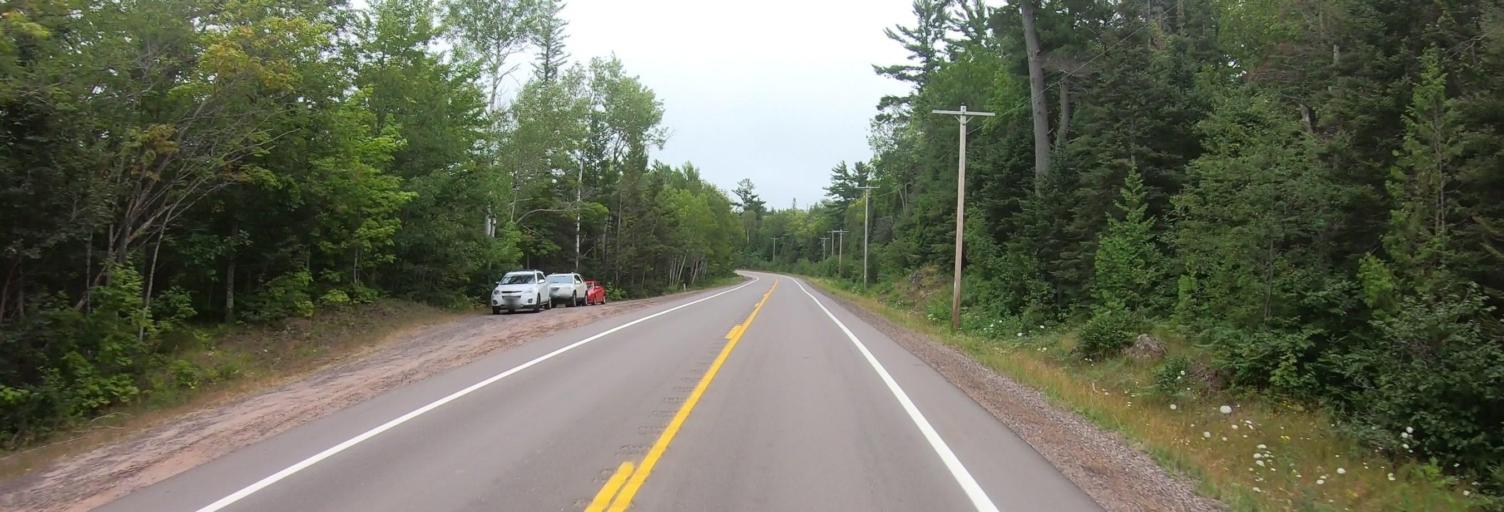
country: US
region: Michigan
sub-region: Keweenaw County
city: Eagle River
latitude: 47.3975
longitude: -88.2852
